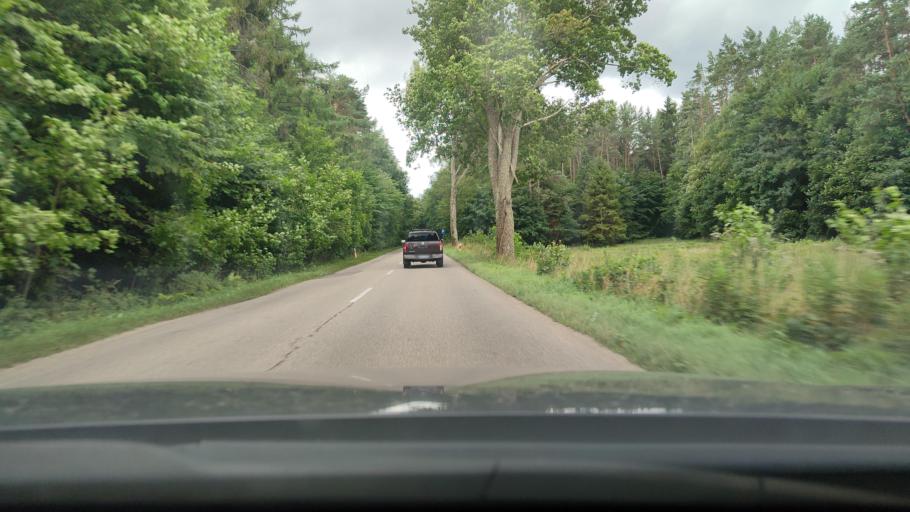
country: PL
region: Pomeranian Voivodeship
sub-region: Powiat pucki
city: Krokowa
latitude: 54.7277
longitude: 18.1700
